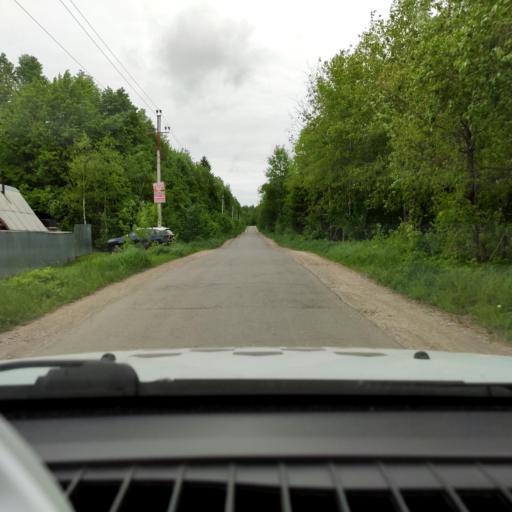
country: RU
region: Perm
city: Novyye Lyady
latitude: 58.0432
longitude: 56.6189
